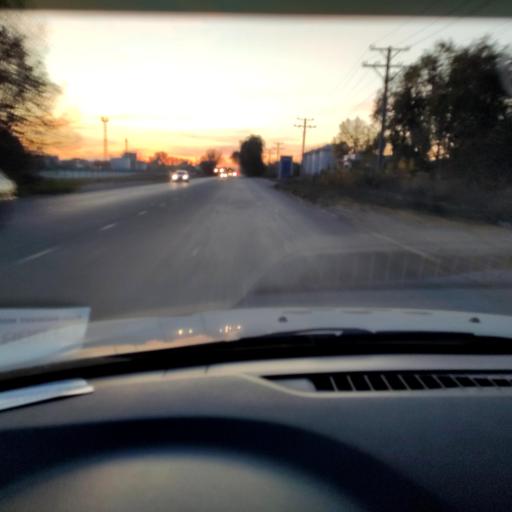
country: RU
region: Samara
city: Tol'yatti
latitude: 53.5326
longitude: 49.4539
